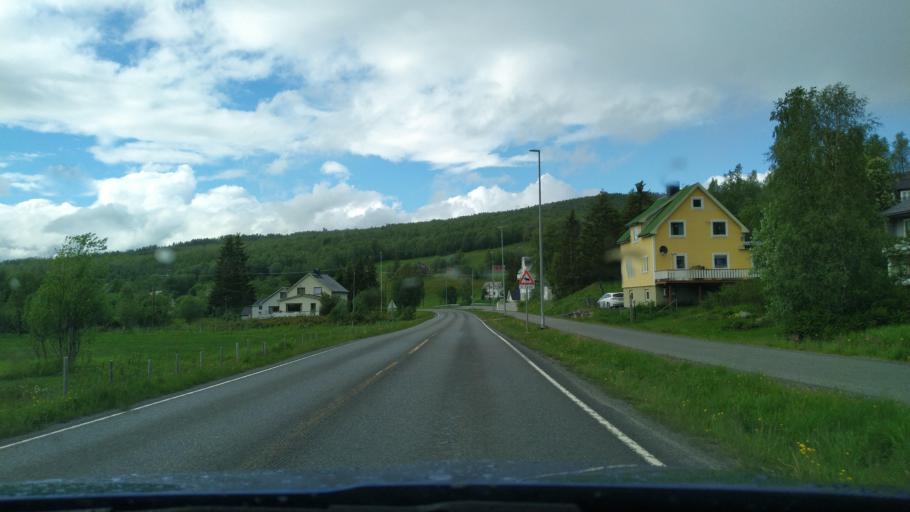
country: NO
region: Troms
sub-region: Sorreisa
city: Sorreisa
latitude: 69.1706
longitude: 18.1144
